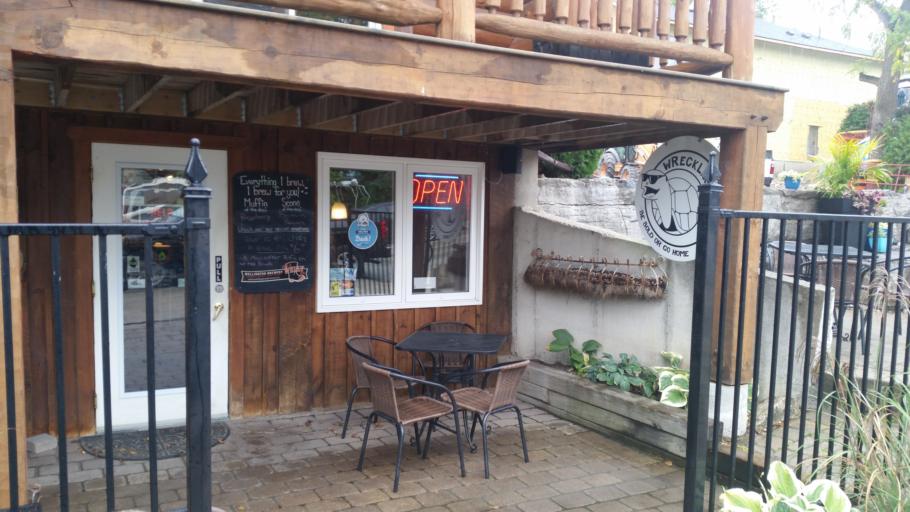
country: CA
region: Ontario
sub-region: Wellington County
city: Guelph
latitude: 43.6819
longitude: -80.4300
